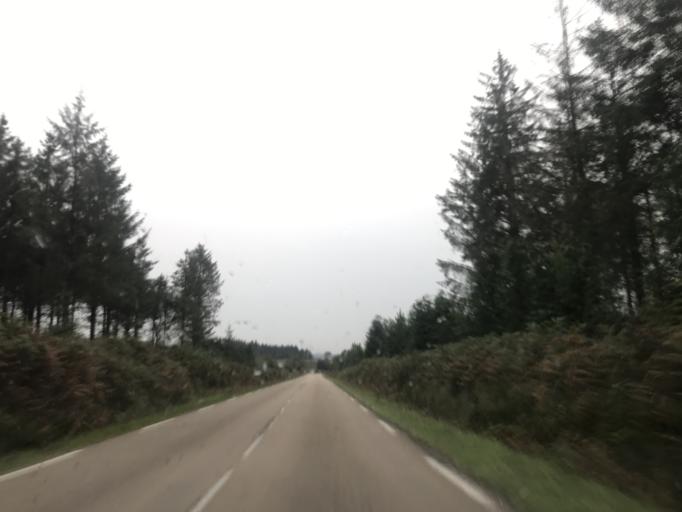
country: FR
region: Brittany
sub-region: Departement du Finistere
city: Plouneour-Menez
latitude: 48.4036
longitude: -3.9352
